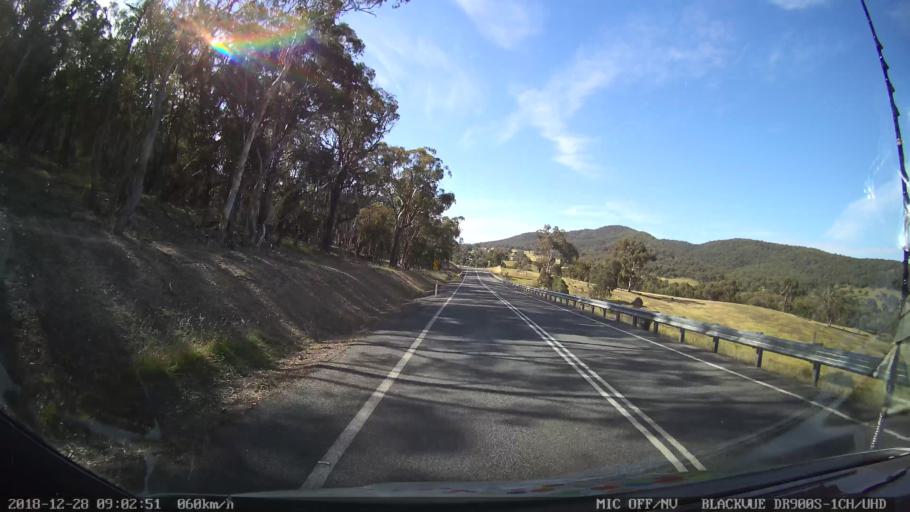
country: AU
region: New South Wales
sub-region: Upper Lachlan Shire
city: Crookwell
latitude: -34.1580
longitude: 149.3351
